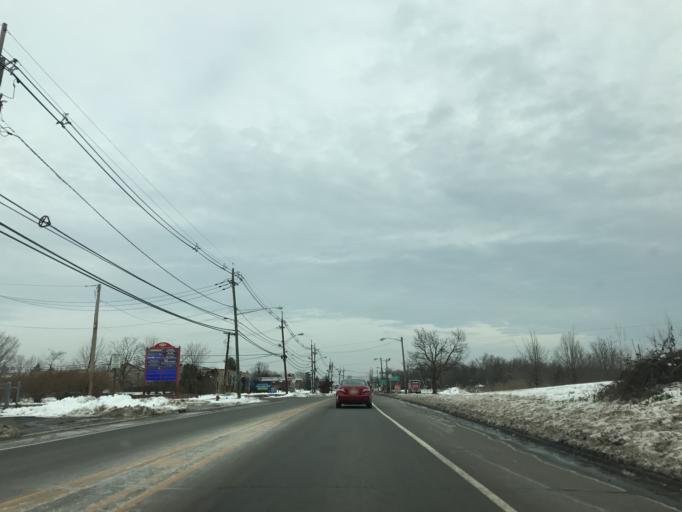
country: US
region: New Jersey
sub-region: Somerset County
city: Weston
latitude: 40.5358
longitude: -74.6183
